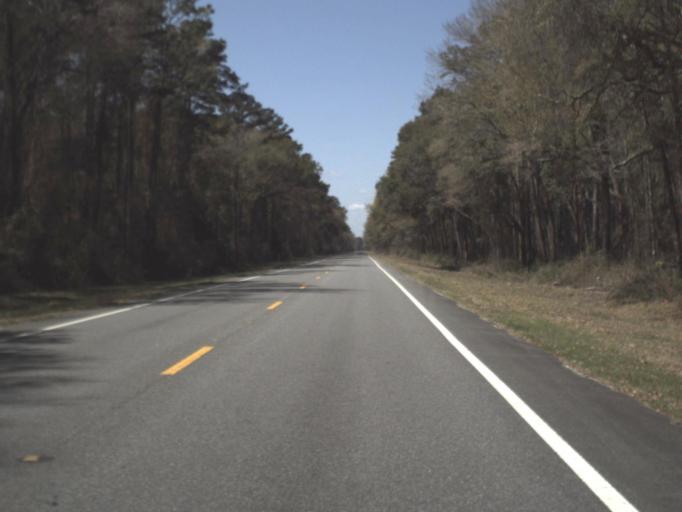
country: US
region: Florida
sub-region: Leon County
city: Woodville
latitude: 30.2431
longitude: -84.2925
